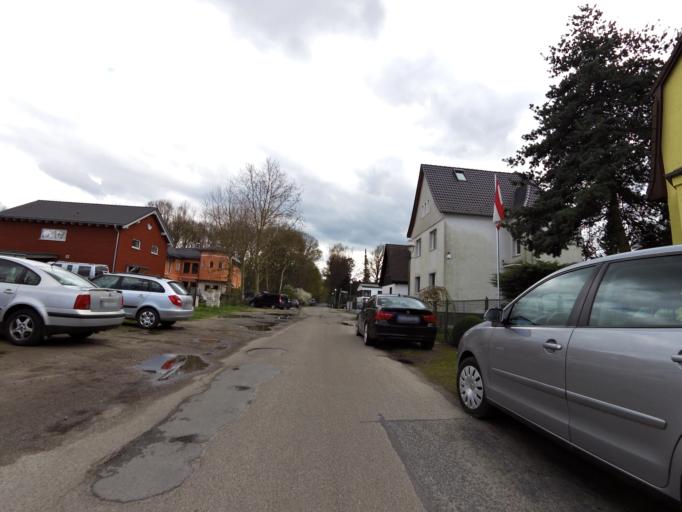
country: DE
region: Berlin
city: Lichtenrade
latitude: 52.3818
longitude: 13.4097
